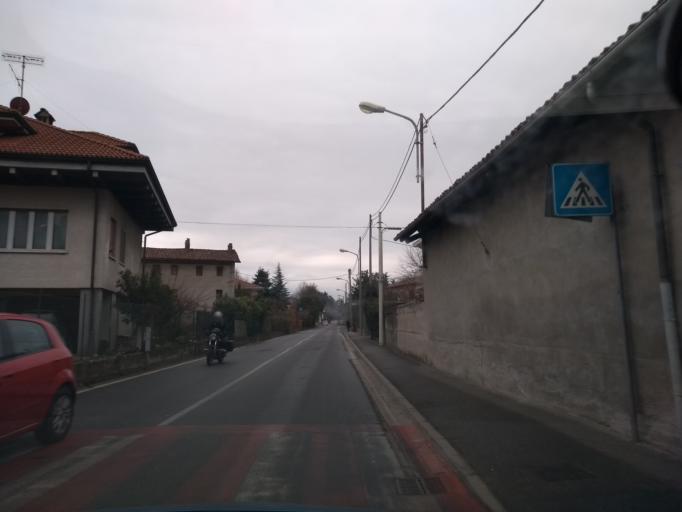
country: IT
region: Piedmont
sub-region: Provincia di Torino
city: Banchette
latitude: 45.4596
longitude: 7.8608
